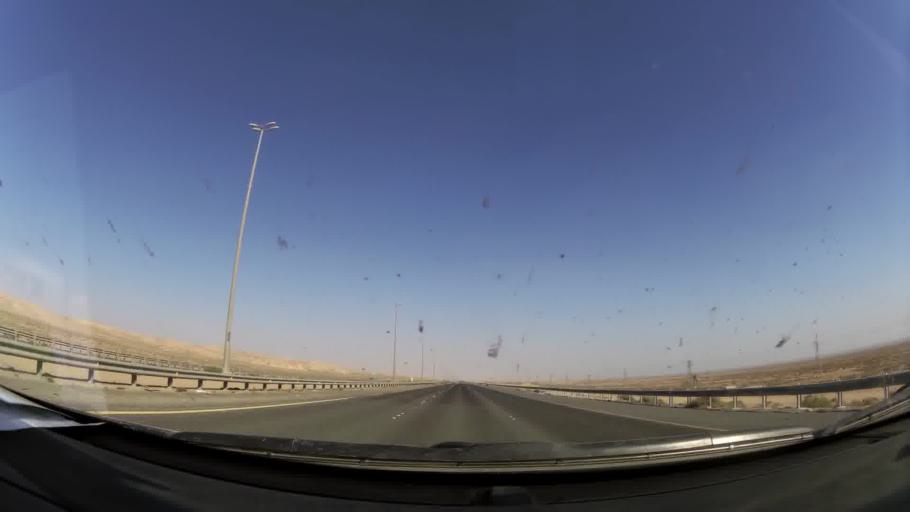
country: KW
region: Al Asimah
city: Kuwait City
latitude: 29.5362
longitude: 47.8412
